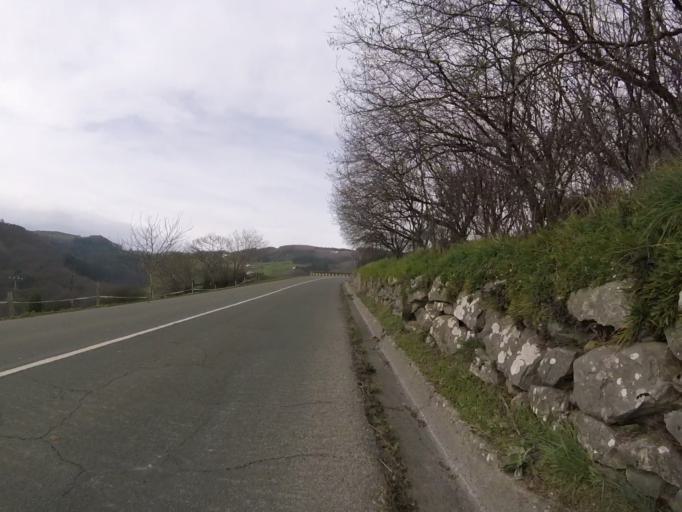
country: ES
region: Basque Country
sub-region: Provincia de Guipuzcoa
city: Errezil
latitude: 43.1431
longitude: -2.1717
